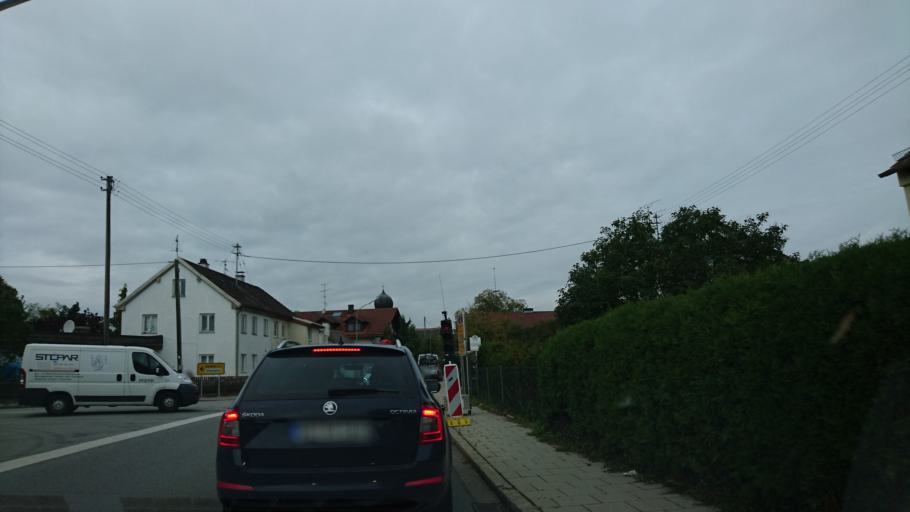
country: DE
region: Bavaria
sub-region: Upper Bavaria
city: Vaterstetten
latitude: 48.1322
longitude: 11.7673
